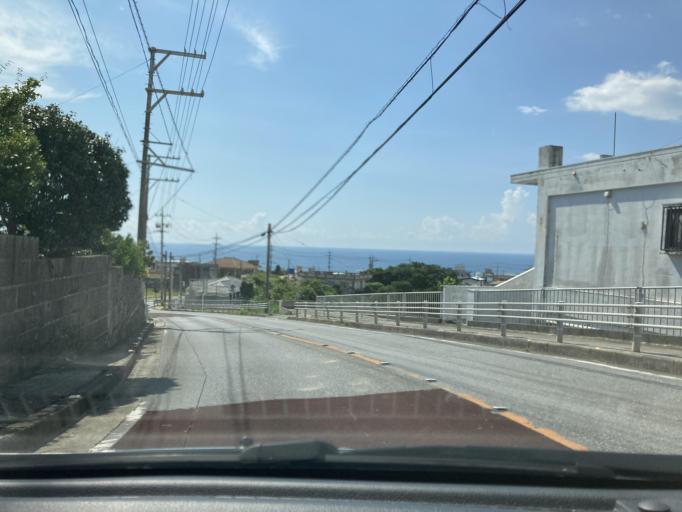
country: JP
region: Okinawa
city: Tomigusuku
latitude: 26.1436
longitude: 127.7920
